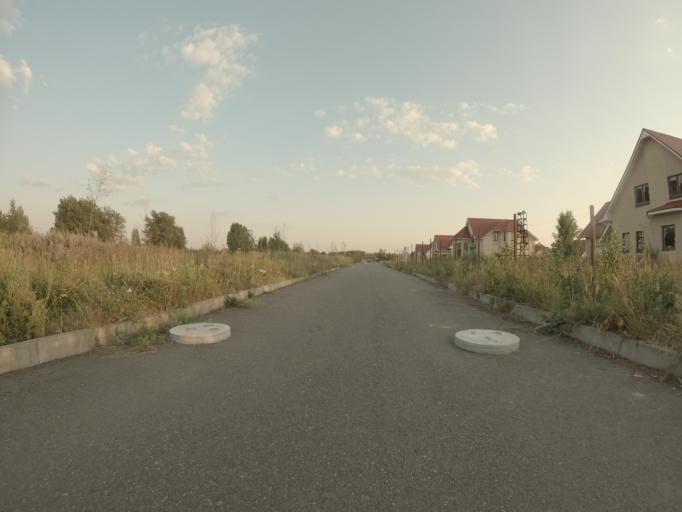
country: RU
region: Leningrad
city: Kirovsk
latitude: 59.8520
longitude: 30.9466
